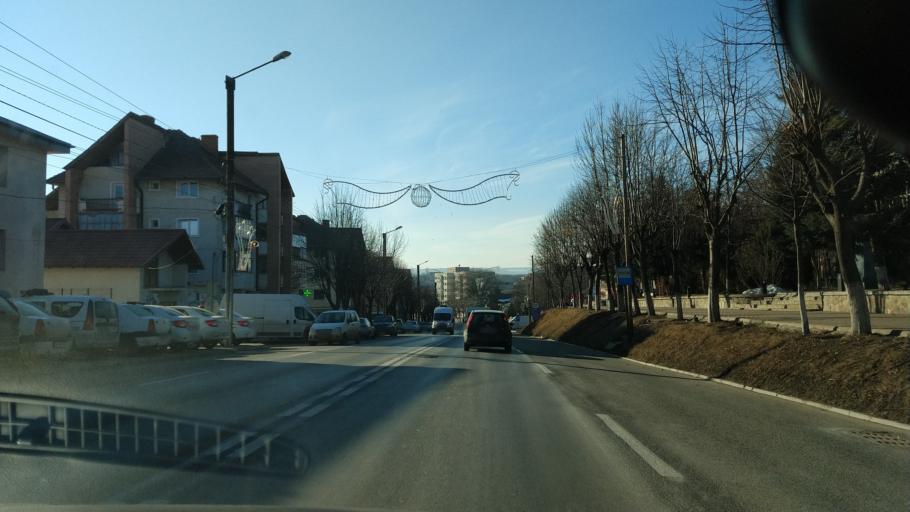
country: RO
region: Iasi
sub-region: Comuna Ion Neculce
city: Buznea
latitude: 47.2088
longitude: 27.0152
